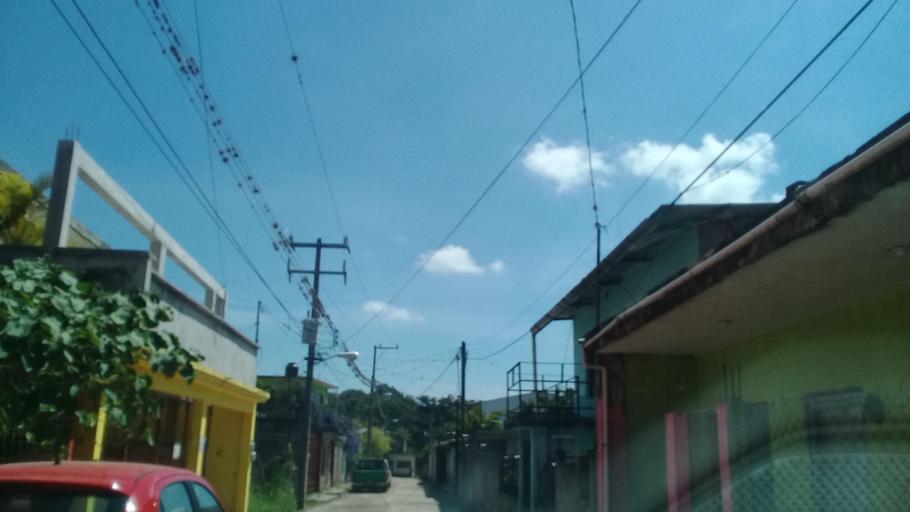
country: MX
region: Veracruz
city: Amatlan de los Reyes
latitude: 18.8413
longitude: -96.9168
